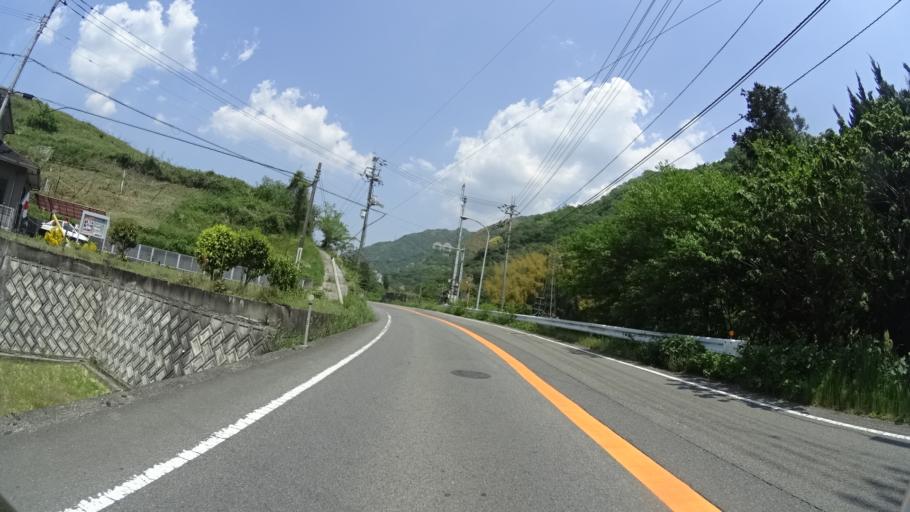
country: JP
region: Ehime
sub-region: Shikoku-chuo Shi
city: Matsuyama
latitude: 33.8633
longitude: 132.8208
